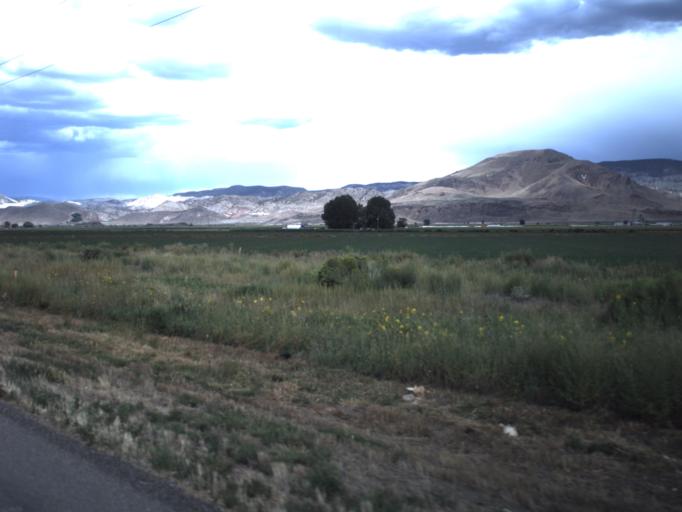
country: US
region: Utah
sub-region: Sevier County
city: Richfield
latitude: 38.8090
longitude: -112.0187
